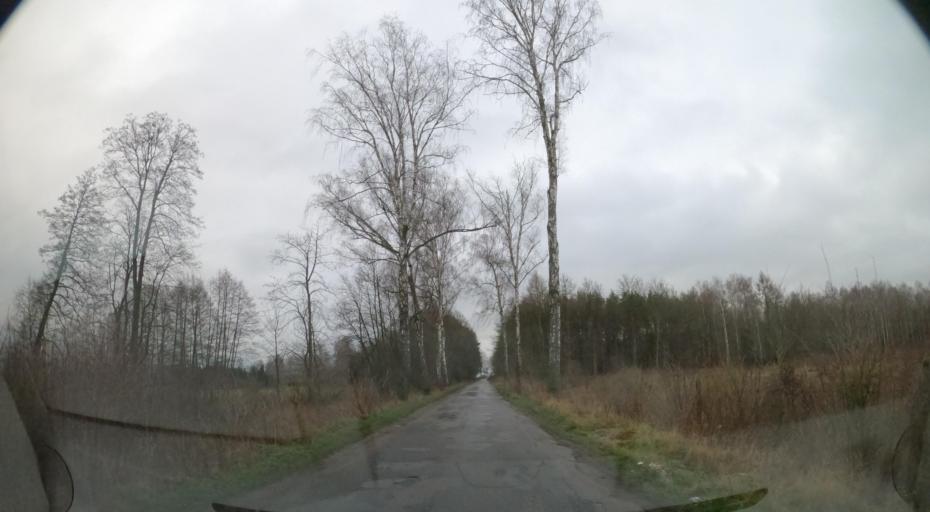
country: PL
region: Greater Poland Voivodeship
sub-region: Powiat zlotowski
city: Zlotow
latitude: 53.2806
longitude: 17.0832
